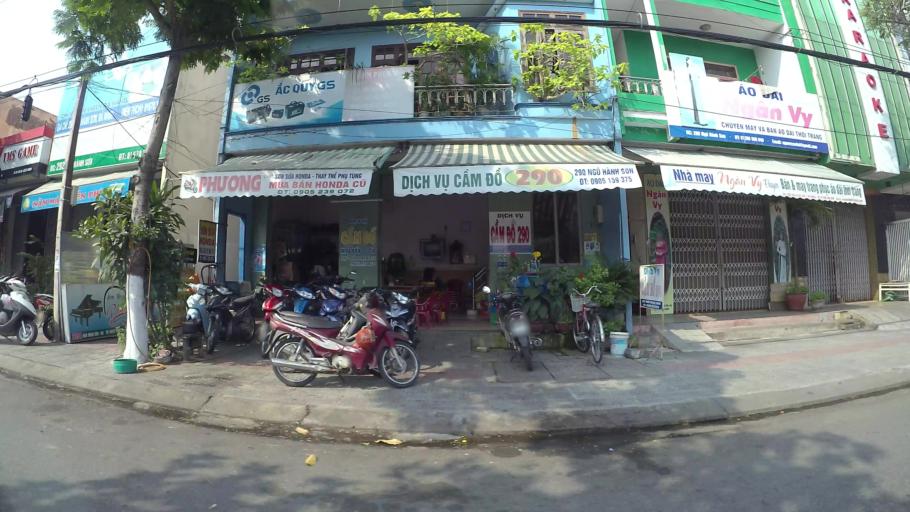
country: VN
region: Da Nang
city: Son Tra
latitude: 16.0435
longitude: 108.2401
